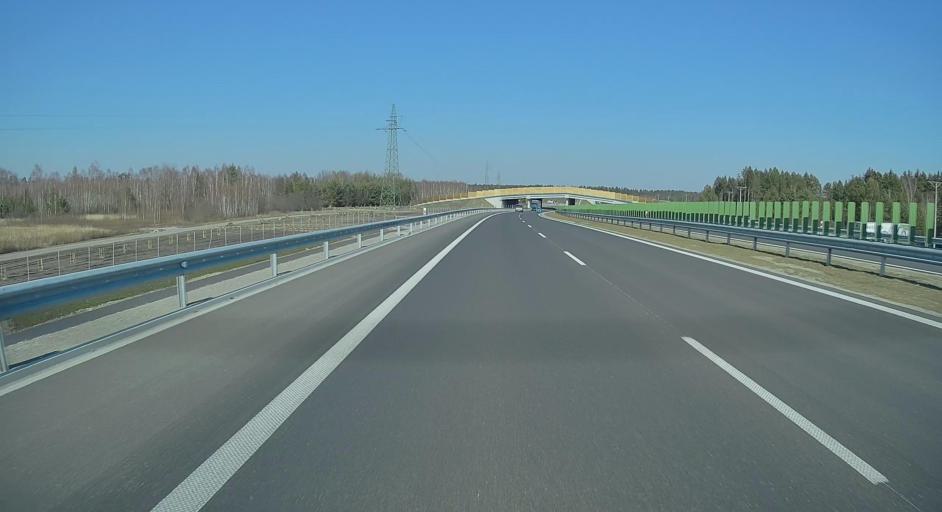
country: PL
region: Subcarpathian Voivodeship
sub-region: Powiat nizanski
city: Konczyce
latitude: 50.4186
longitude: 22.1297
